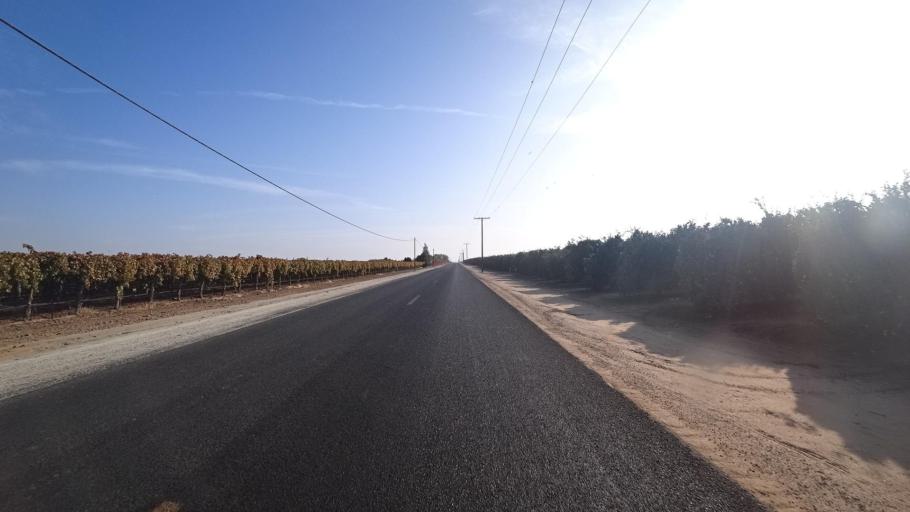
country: US
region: California
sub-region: Kern County
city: McFarland
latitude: 35.6746
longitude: -119.1758
